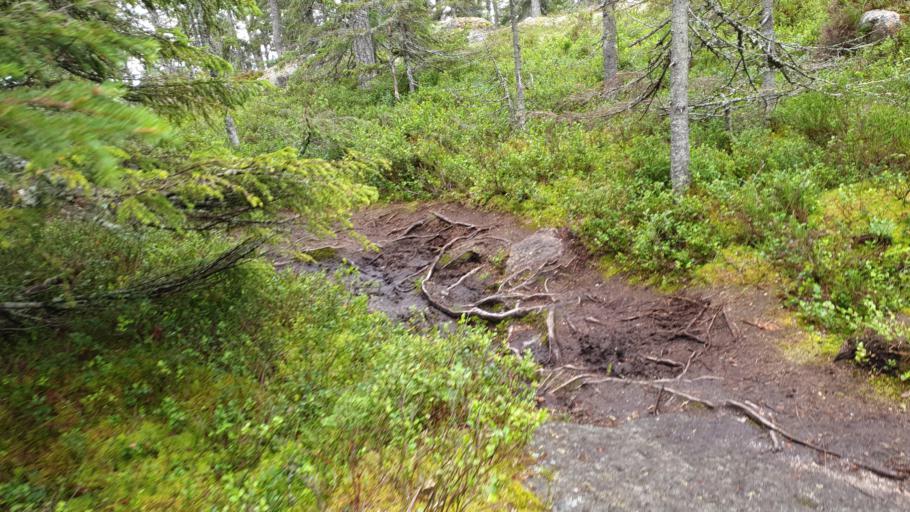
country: SE
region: Gaevleborg
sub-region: Hudiksvalls Kommun
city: Sorforsa
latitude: 61.6435
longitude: 16.7651
